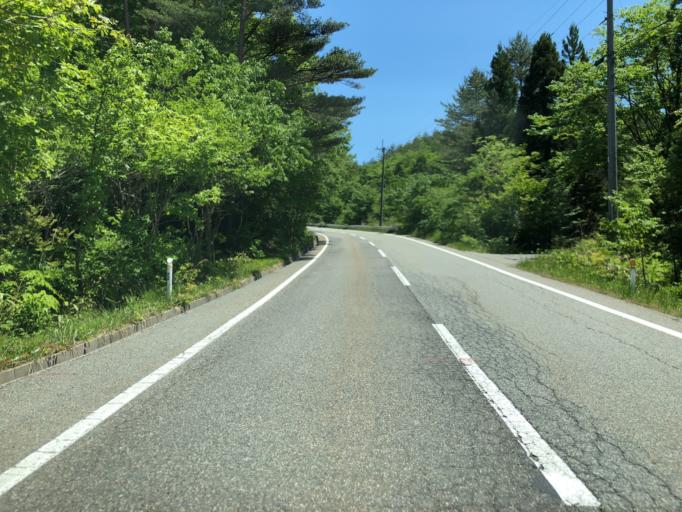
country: JP
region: Fukushima
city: Namie
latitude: 37.5215
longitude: 140.7871
